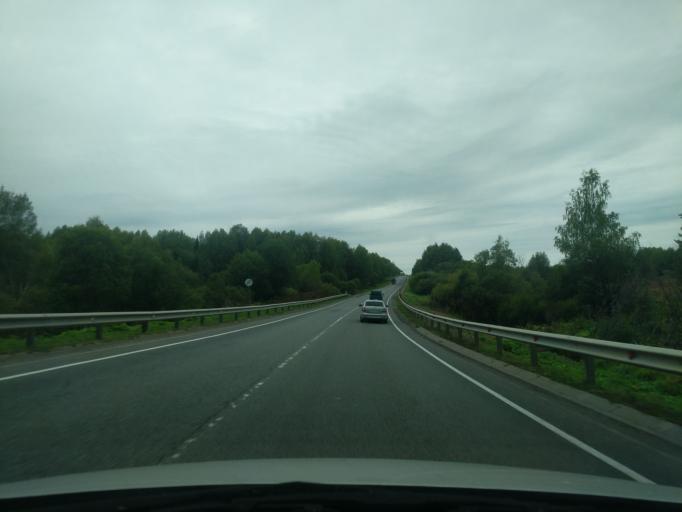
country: RU
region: Kirov
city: Orlov
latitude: 58.5377
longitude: 48.7967
